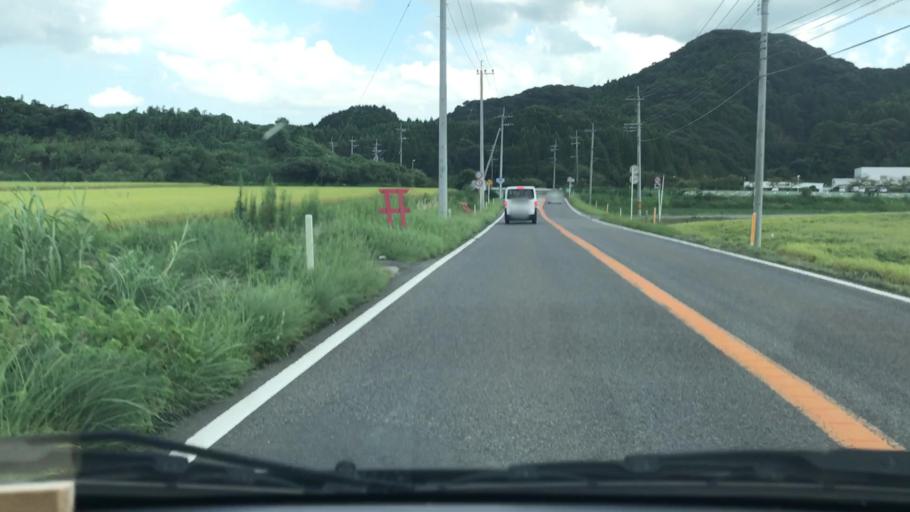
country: JP
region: Saga Prefecture
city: Takeocho-takeo
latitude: 33.2251
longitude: 130.0312
